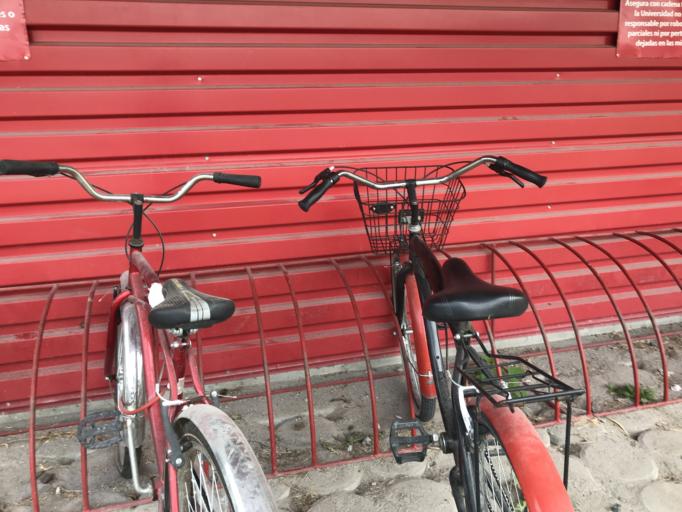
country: MX
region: Puebla
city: Tlazcalancingo
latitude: 19.0300
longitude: -98.2423
